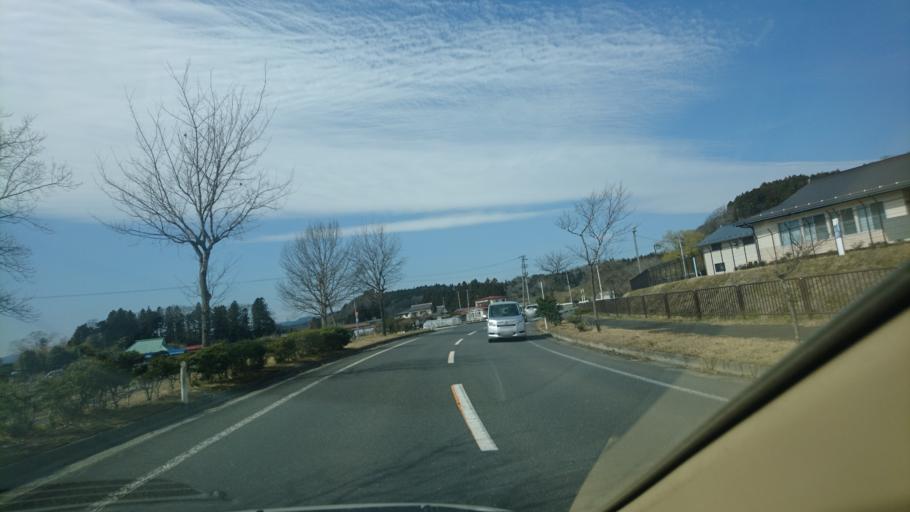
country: JP
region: Miyagi
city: Furukawa
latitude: 38.7453
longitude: 140.9497
